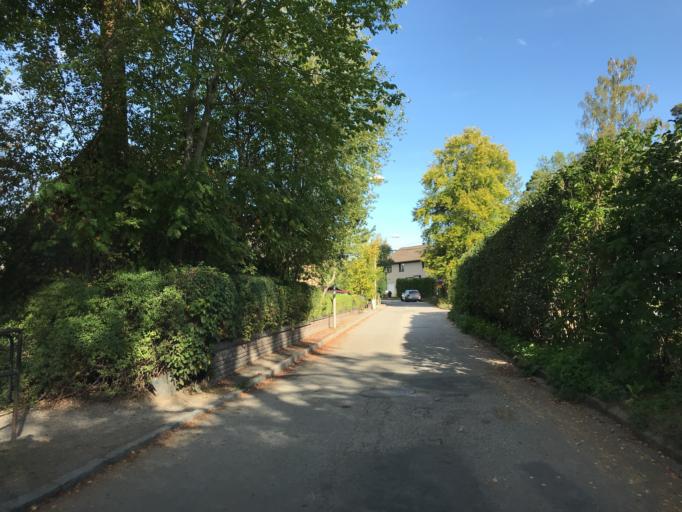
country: SE
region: Stockholm
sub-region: Huddinge Kommun
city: Segeltorp
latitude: 59.2747
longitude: 17.9562
